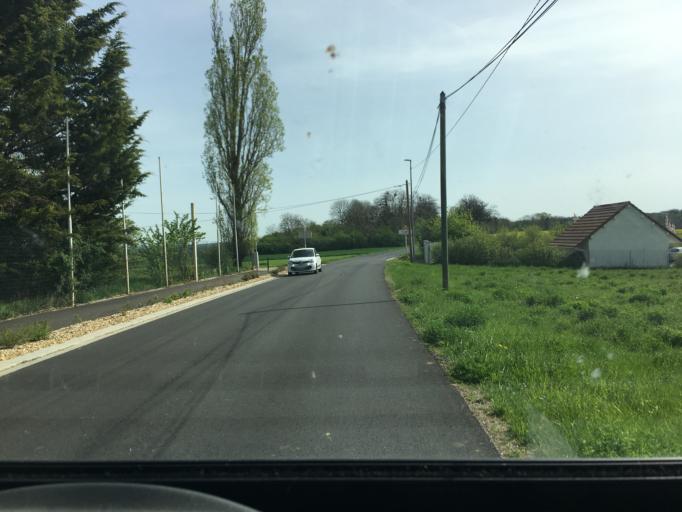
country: FR
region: Lorraine
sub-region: Departement de Meurthe-et-Moselle
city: Gondreville
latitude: 48.6608
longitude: 5.9839
